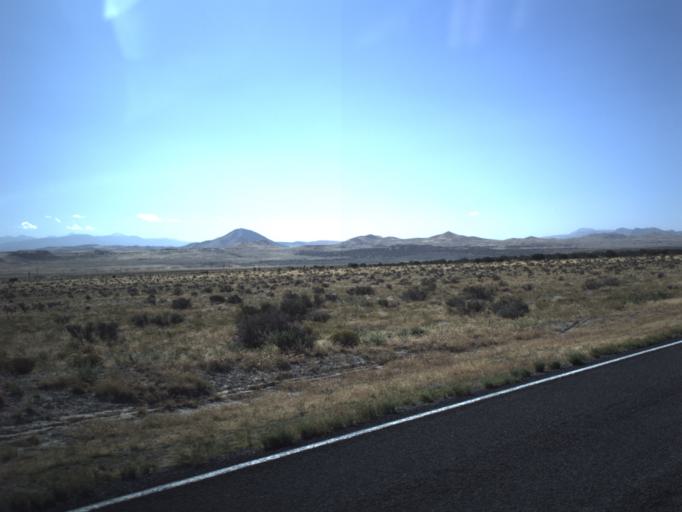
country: US
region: Utah
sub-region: Beaver County
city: Milford
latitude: 38.8476
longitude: -112.8433
